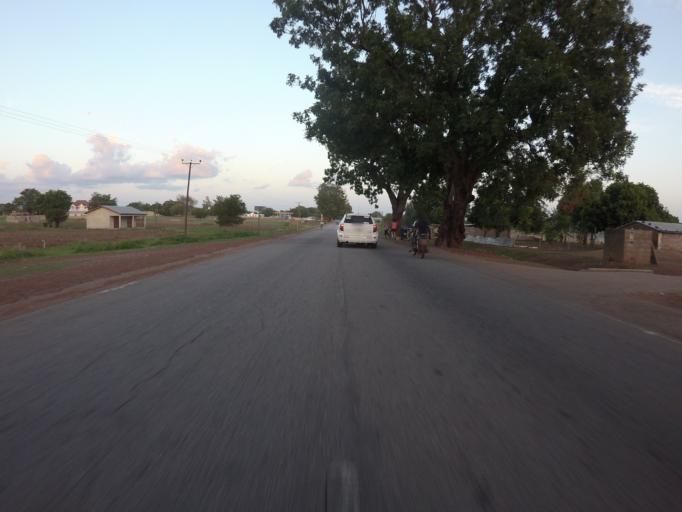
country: GH
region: Upper East
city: Navrongo
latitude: 10.8578
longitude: -1.0280
